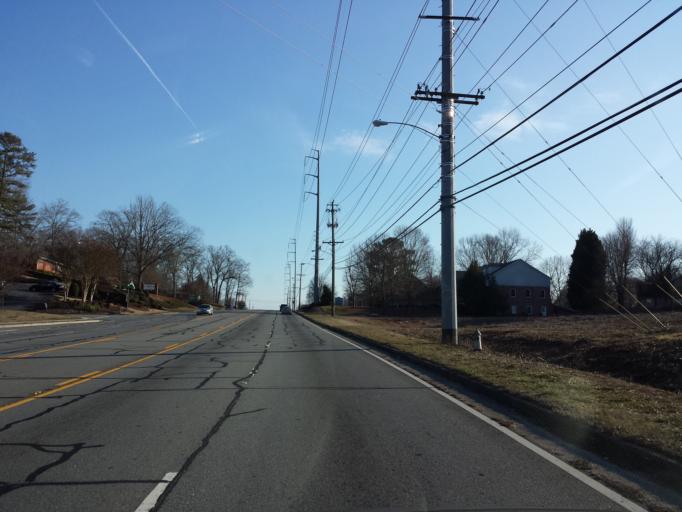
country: US
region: Georgia
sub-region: Cherokee County
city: Woodstock
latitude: 34.0442
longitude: -84.5297
